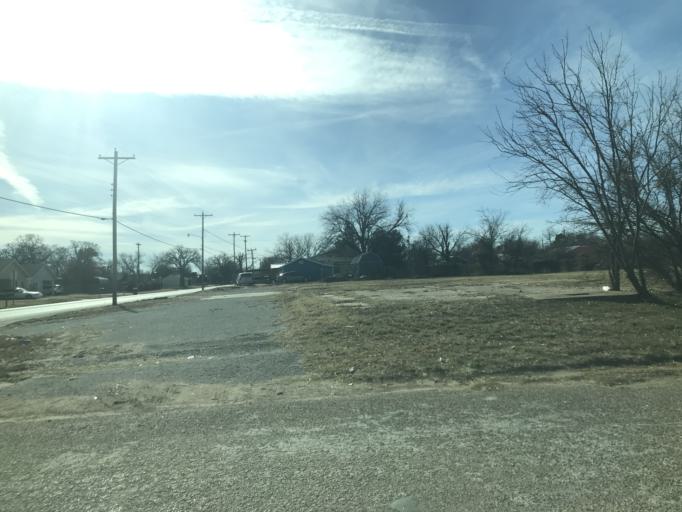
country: US
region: Texas
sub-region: Taylor County
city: Abilene
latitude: 32.4879
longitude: -99.7396
